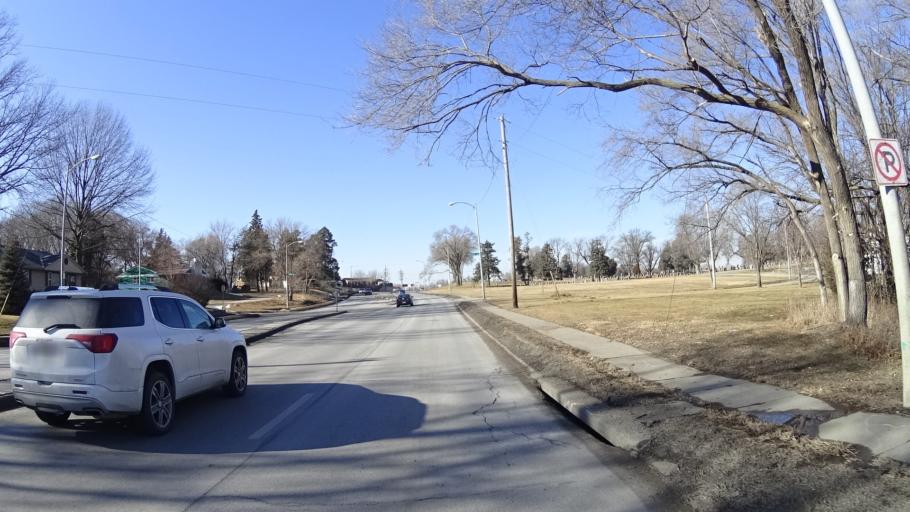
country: US
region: Nebraska
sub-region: Douglas County
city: Ralston
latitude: 41.3009
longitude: -96.0301
